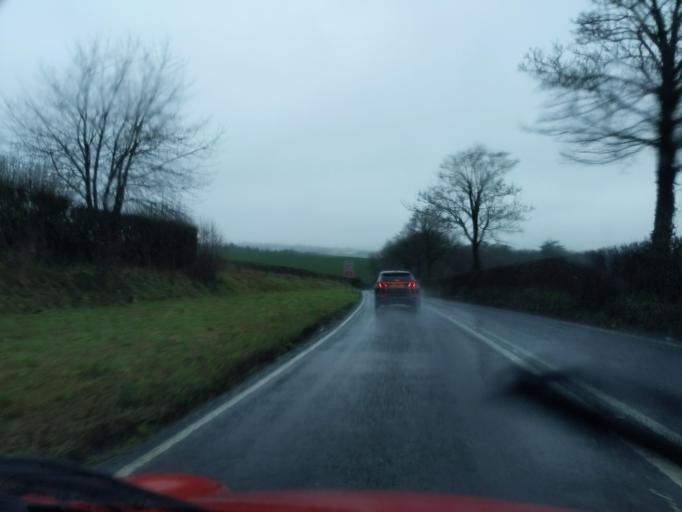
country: GB
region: England
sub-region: Cornwall
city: South Hill
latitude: 50.5549
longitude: -4.3307
